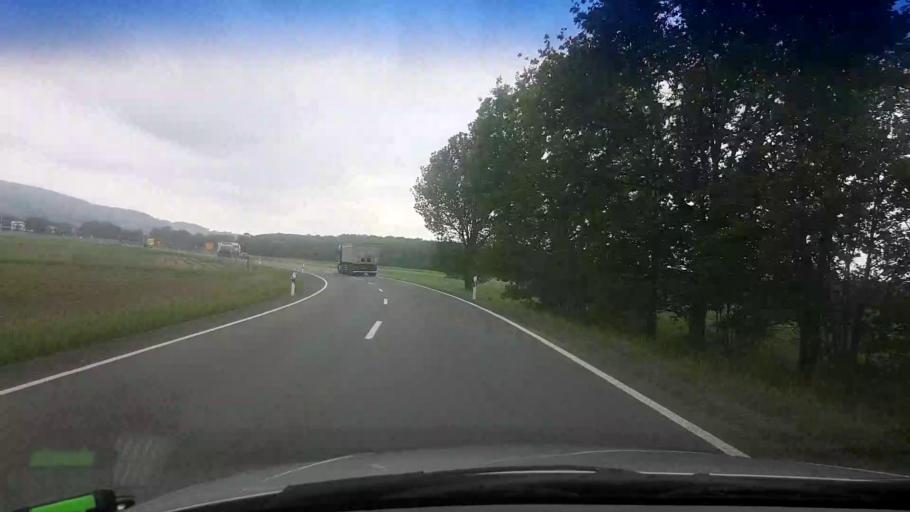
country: DE
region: Bavaria
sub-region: Upper Franconia
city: Gesees
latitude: 50.0185
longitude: 11.6641
